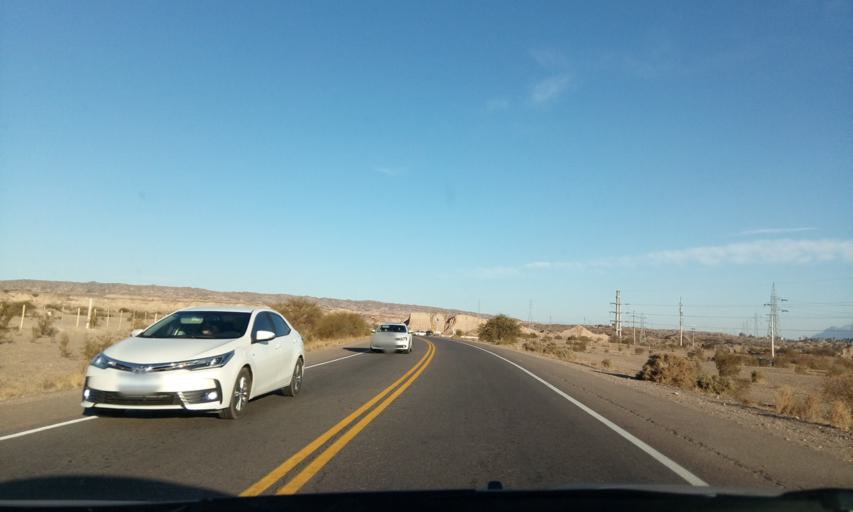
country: AR
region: San Juan
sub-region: Departamento de Rivadavia
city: Rivadavia
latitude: -31.4430
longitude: -68.6529
